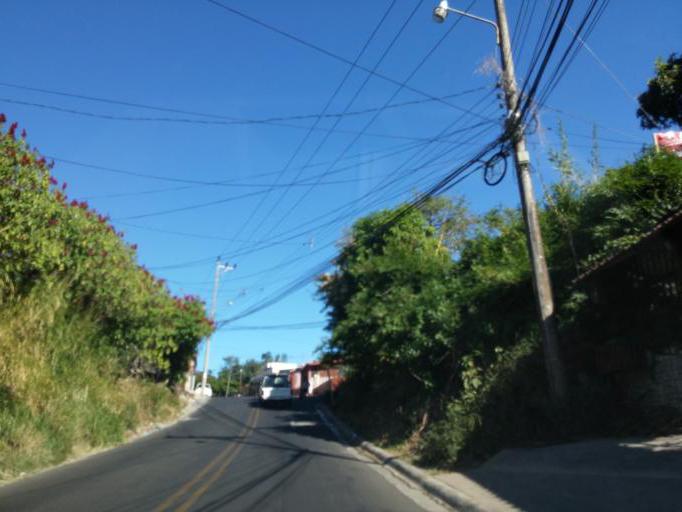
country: CR
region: Alajuela
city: Alajuela
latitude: 10.0197
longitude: -84.1865
